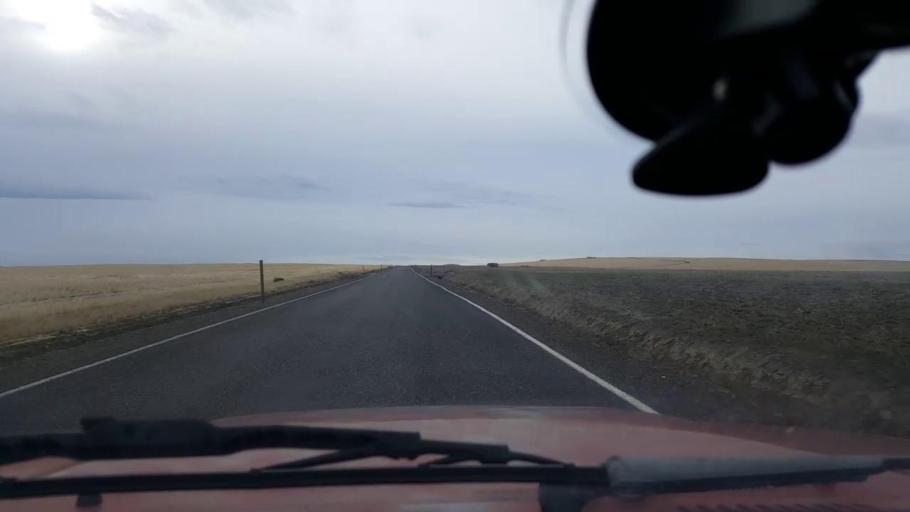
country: US
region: Washington
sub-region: Asotin County
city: Clarkston Heights-Vineland
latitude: 46.3515
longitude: -117.2311
